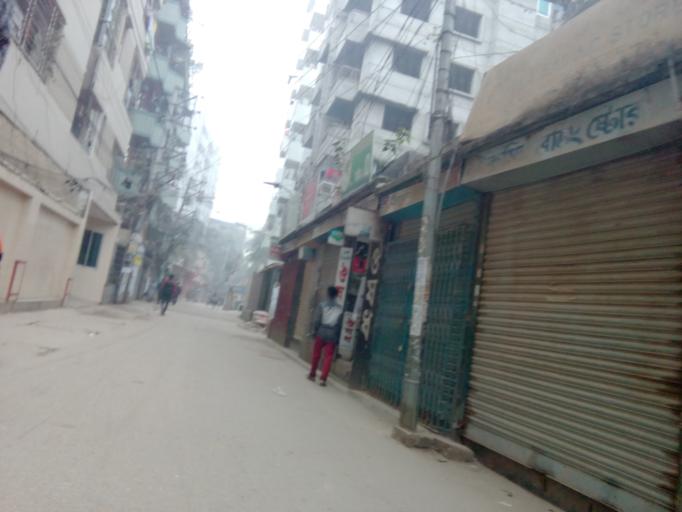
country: BD
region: Dhaka
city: Paltan
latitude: 23.7460
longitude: 90.4141
